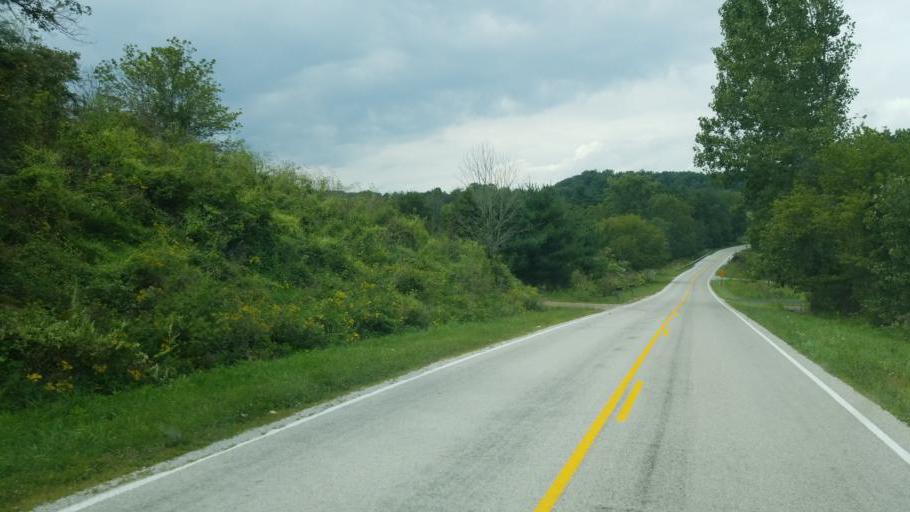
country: US
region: Ohio
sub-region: Sandusky County
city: Bellville
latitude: 40.6289
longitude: -82.3804
